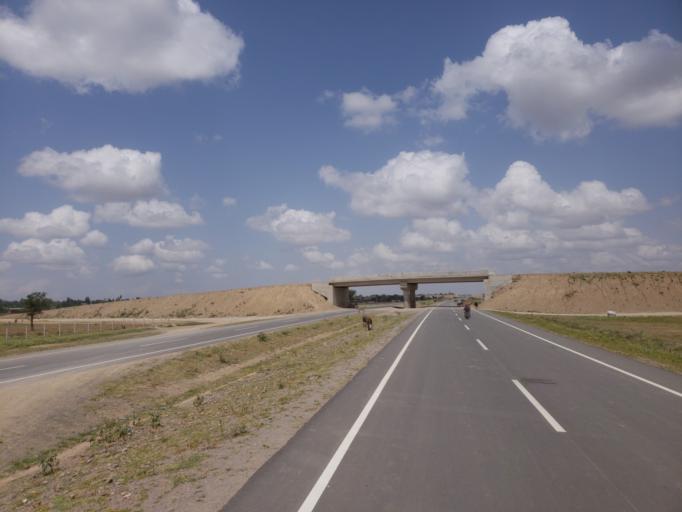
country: ET
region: Oromiya
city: Mojo
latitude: 8.3123
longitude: 38.9474
